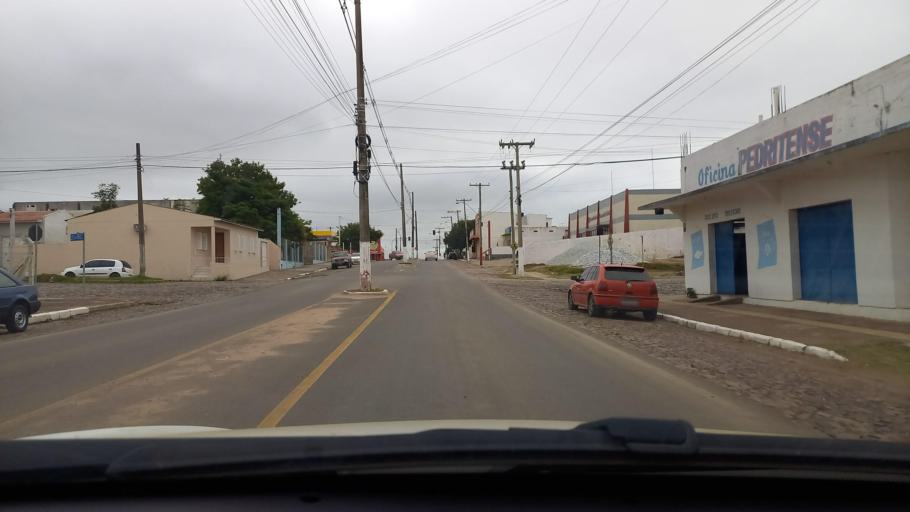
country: BR
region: Rio Grande do Sul
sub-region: Dom Pedrito
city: Dom Pedrito
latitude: -30.9818
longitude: -54.6664
